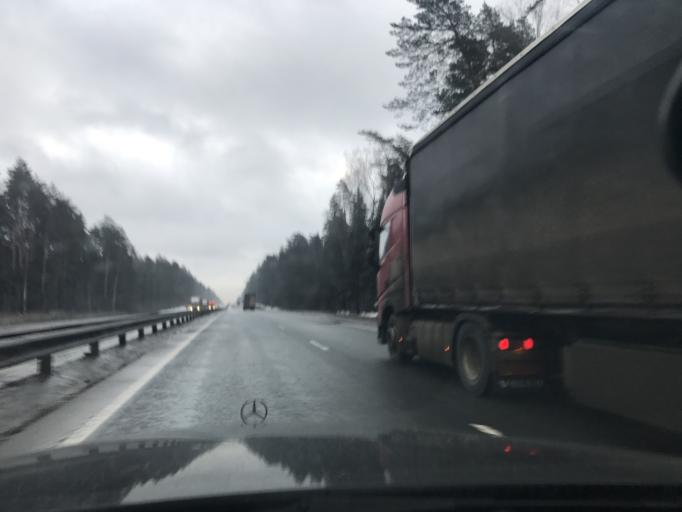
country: RU
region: Vladimir
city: Kameshkovo
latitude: 56.1979
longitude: 41.0263
